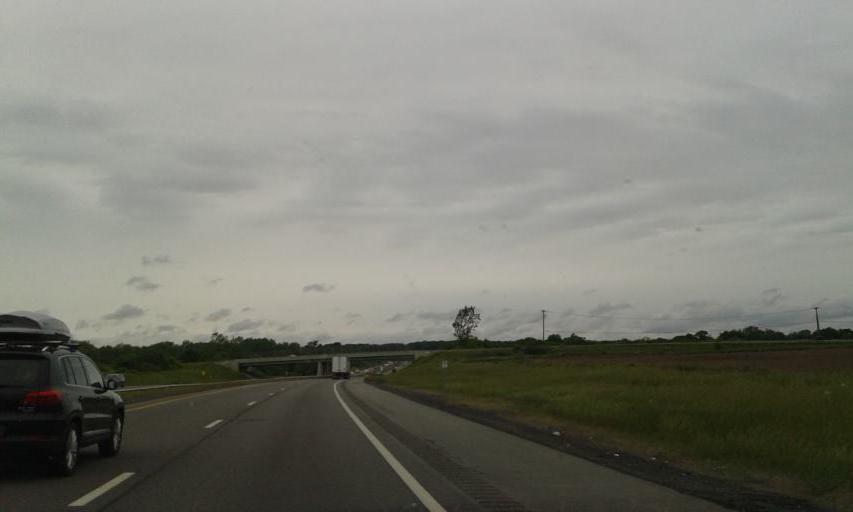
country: US
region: New York
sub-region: Genesee County
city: Batavia
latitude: 43.0148
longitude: -78.1087
